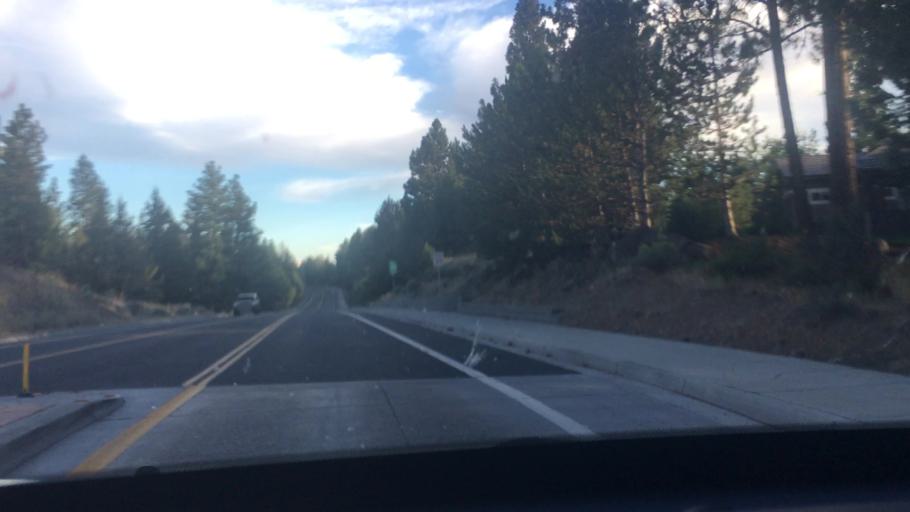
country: US
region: Oregon
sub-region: Deschutes County
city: Bend
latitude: 44.0467
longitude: -121.3441
